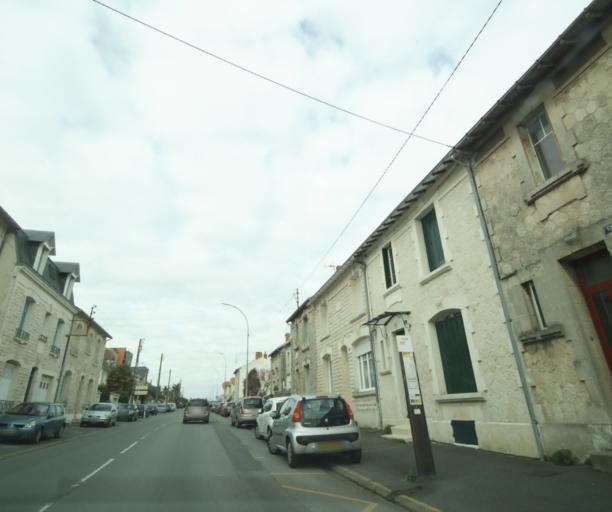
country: FR
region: Poitou-Charentes
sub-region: Departement de la Charente-Maritime
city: La Rochelle
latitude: 46.1638
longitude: -1.1650
